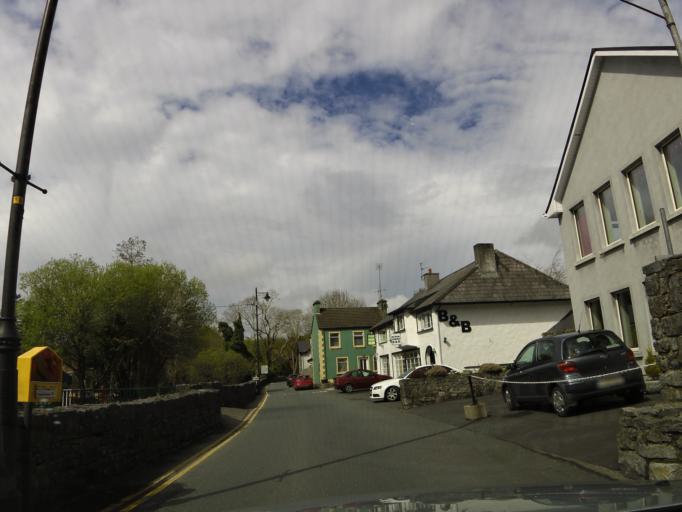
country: IE
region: Connaught
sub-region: Maigh Eo
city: Ballinrobe
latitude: 53.5409
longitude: -9.2882
